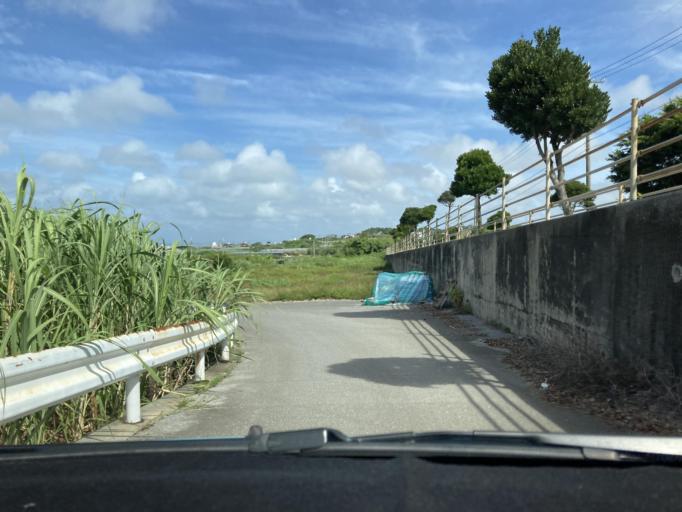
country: JP
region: Okinawa
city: Itoman
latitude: 26.0972
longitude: 127.6656
